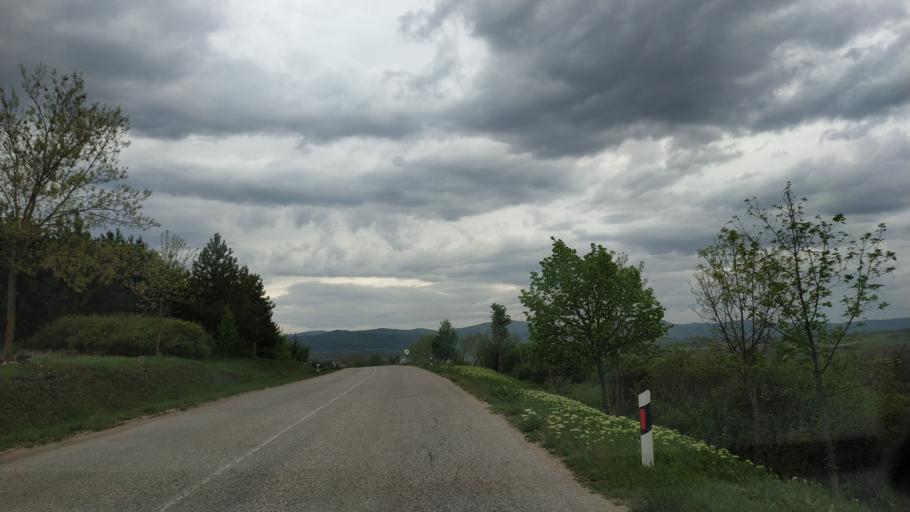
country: RS
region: Central Serbia
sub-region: Zajecarski Okrug
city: Soko Banja
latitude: 43.6548
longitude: 21.8335
